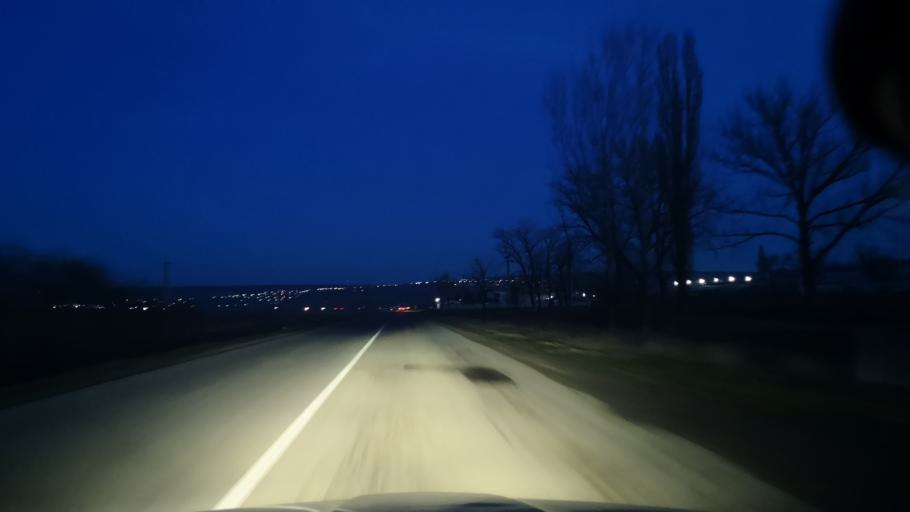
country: MD
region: Orhei
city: Orhei
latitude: 47.3431
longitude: 28.7669
